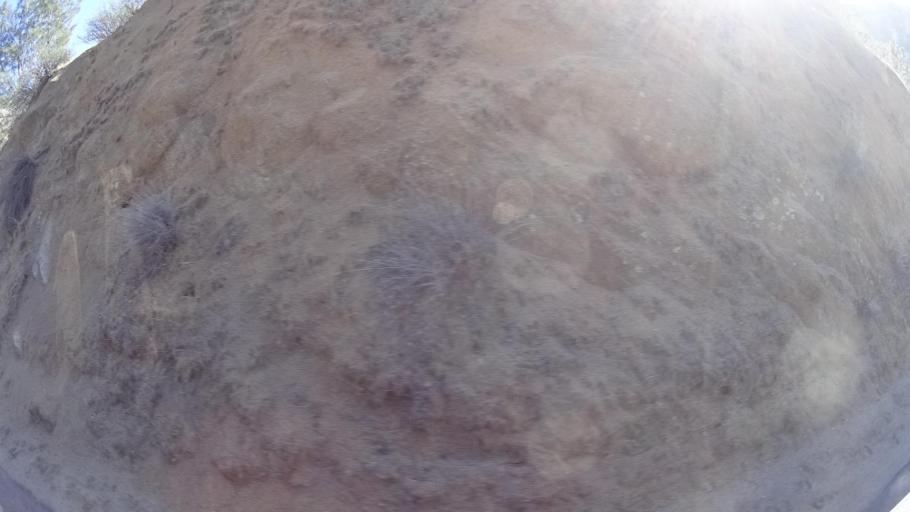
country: US
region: California
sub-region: Kern County
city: Bodfish
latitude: 35.5655
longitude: -118.5706
